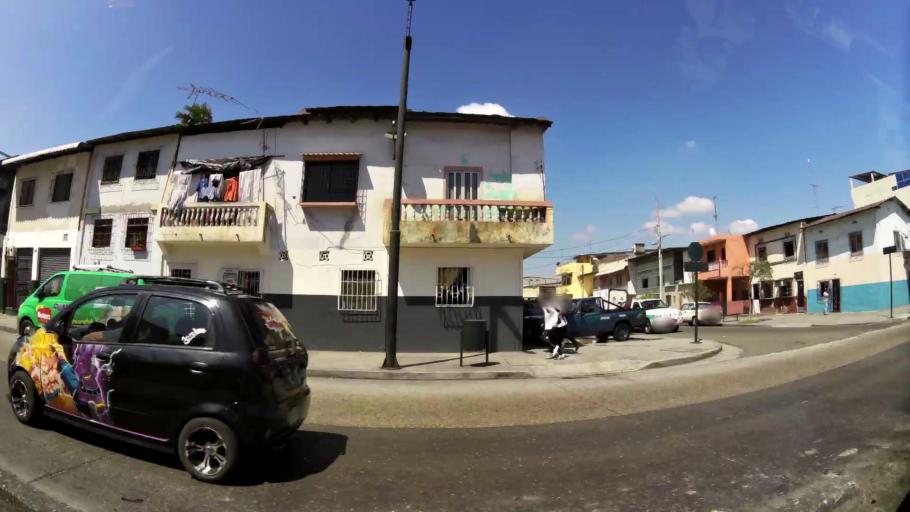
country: EC
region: Guayas
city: Guayaquil
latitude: -2.2032
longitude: -79.9267
